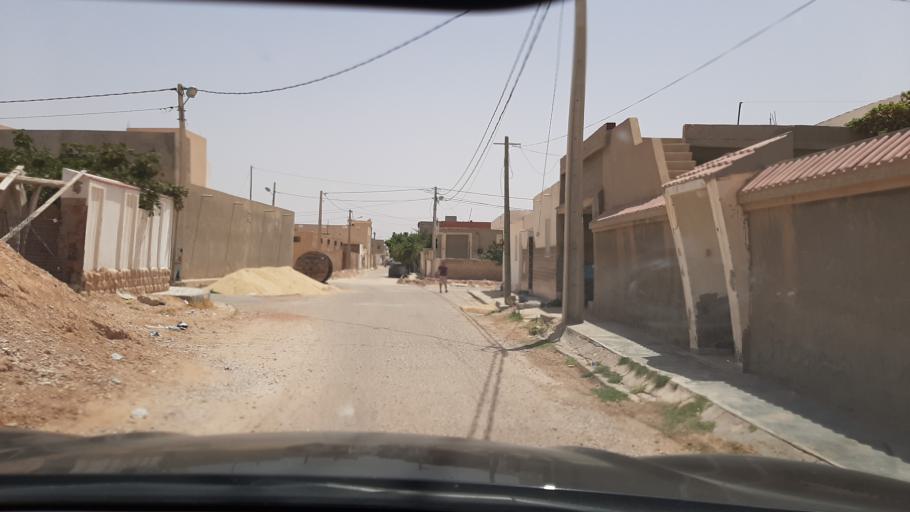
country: TN
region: Qabis
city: Matmata
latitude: 33.6188
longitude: 10.2800
